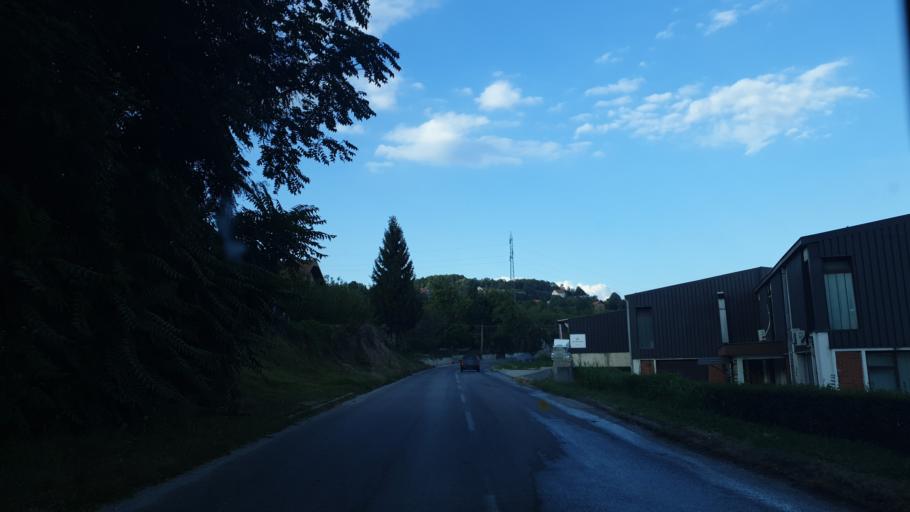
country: RS
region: Central Serbia
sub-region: Zlatiborski Okrug
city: Uzice
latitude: 43.8588
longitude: 19.8778
